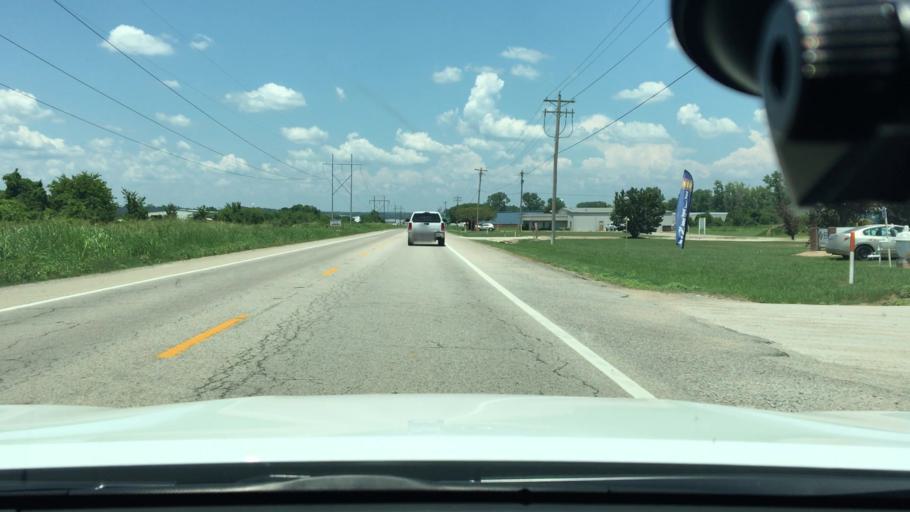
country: US
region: Arkansas
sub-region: Crawford County
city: Van Buren
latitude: 35.4058
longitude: -94.3300
